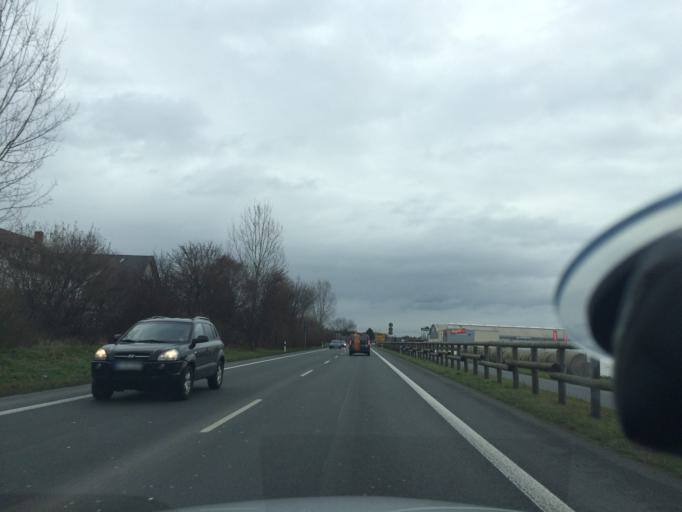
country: DE
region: Hesse
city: Weiterstadt
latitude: 49.8999
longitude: 8.5901
